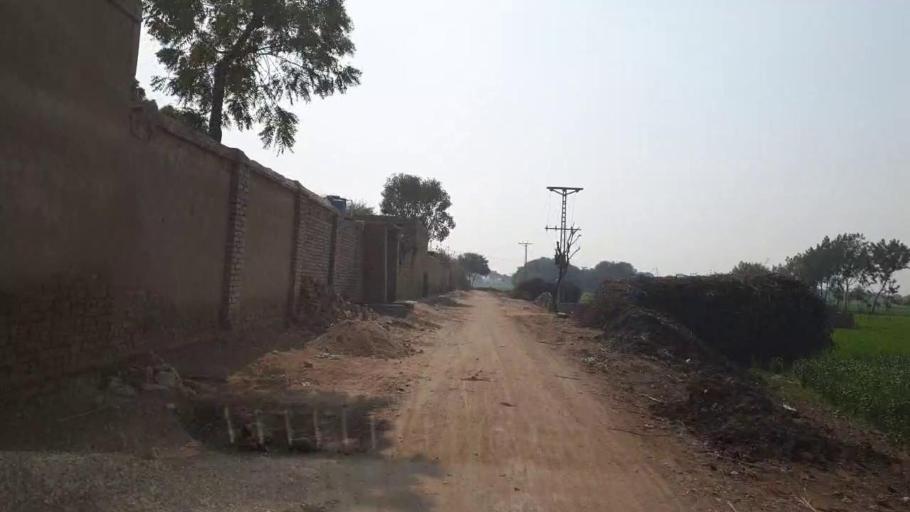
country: PK
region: Sindh
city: Bhit Shah
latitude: 25.7496
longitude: 68.5165
